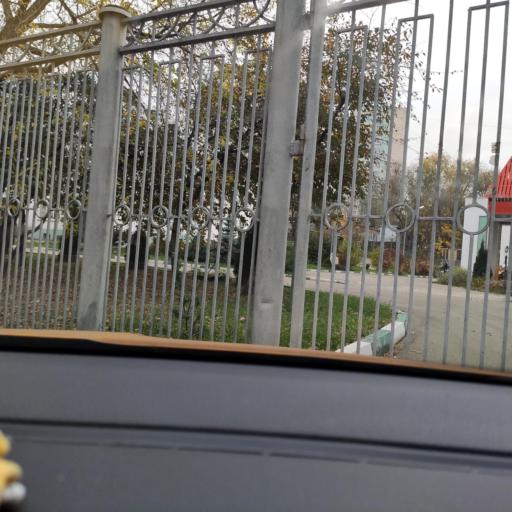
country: RU
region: Moscow
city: Zyuzino
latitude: 55.6641
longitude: 37.5824
